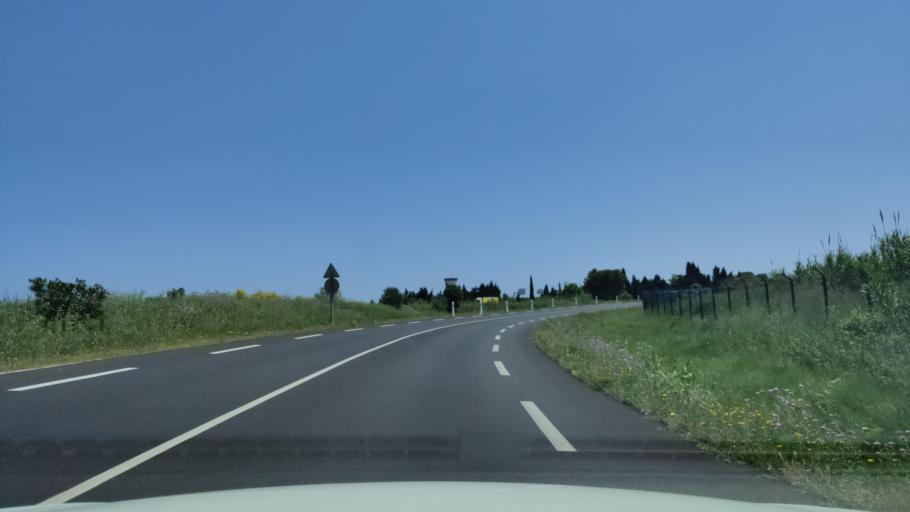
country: FR
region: Languedoc-Roussillon
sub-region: Departement des Pyrenees-Orientales
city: Peyrestortes
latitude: 42.7561
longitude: 2.8609
